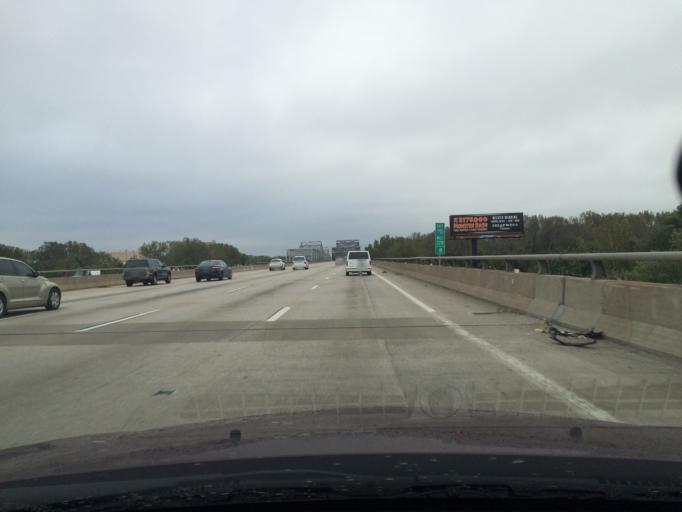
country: US
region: Missouri
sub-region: Saint Charles County
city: Saint Charles
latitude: 38.7667
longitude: -90.4898
